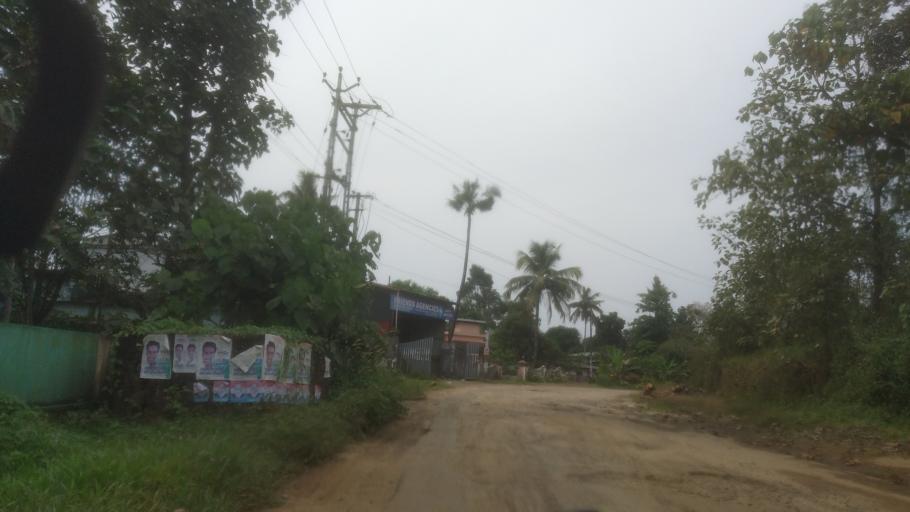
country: IN
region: Kerala
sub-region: Ernakulam
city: Perumbavoor
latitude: 10.0497
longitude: 76.5236
